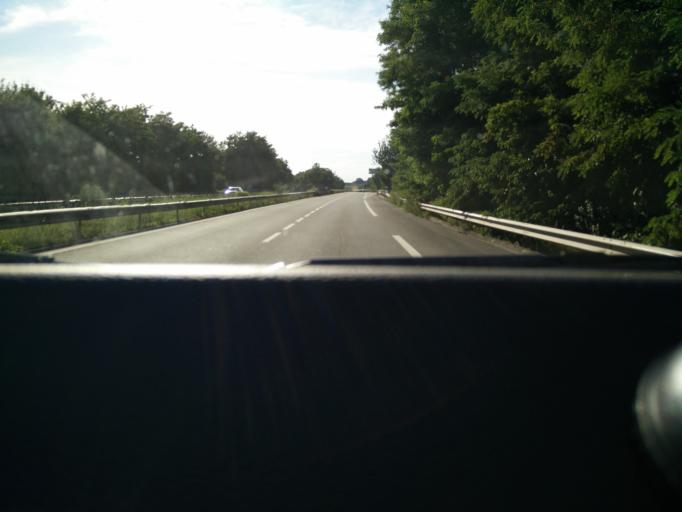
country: FR
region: Nord-Pas-de-Calais
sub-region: Departement du Nord
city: Lourches
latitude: 50.3232
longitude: 3.3500
